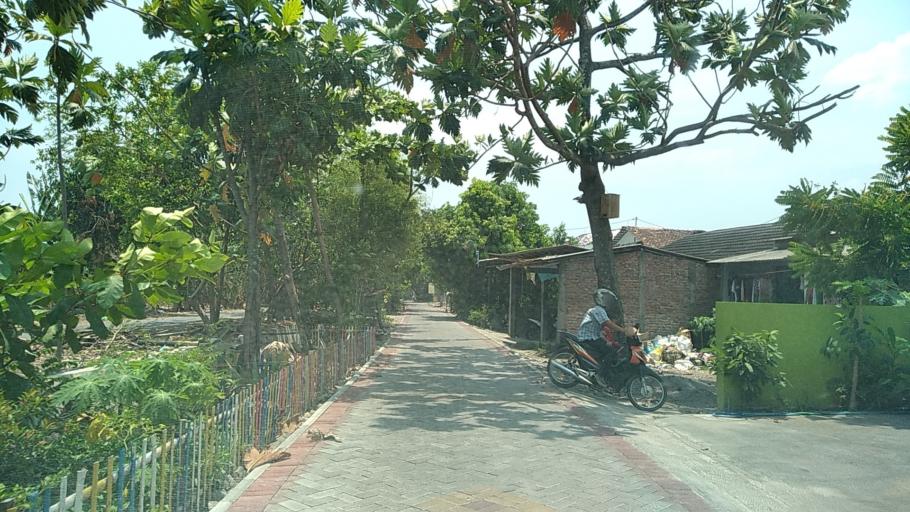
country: ID
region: Central Java
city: Mranggen
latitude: -7.0220
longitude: 110.4773
